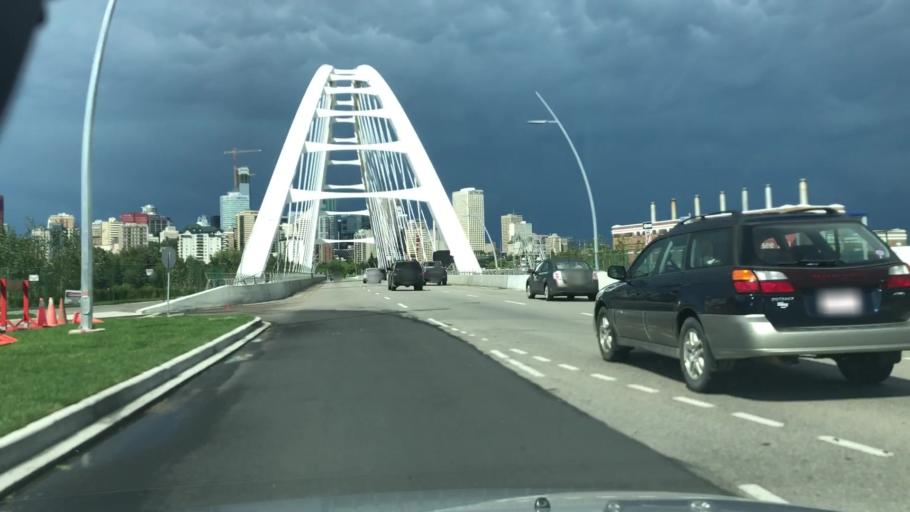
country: CA
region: Alberta
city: Edmonton
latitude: 53.5269
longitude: -113.5027
